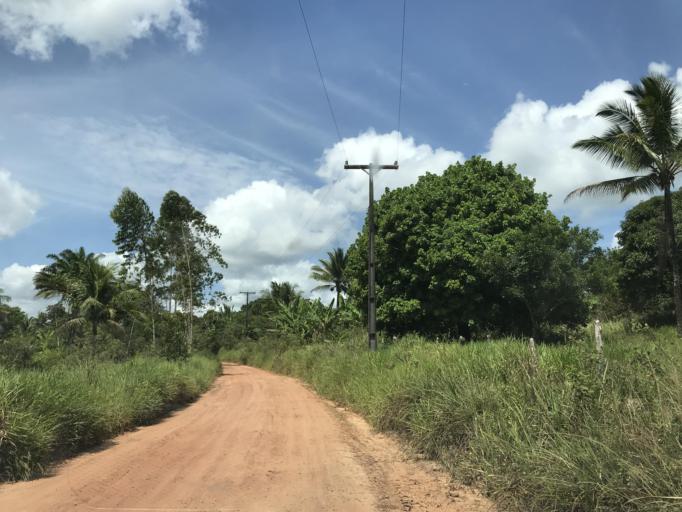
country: BR
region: Bahia
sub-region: Entre Rios
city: Entre Rios
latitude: -12.2223
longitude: -38.0874
